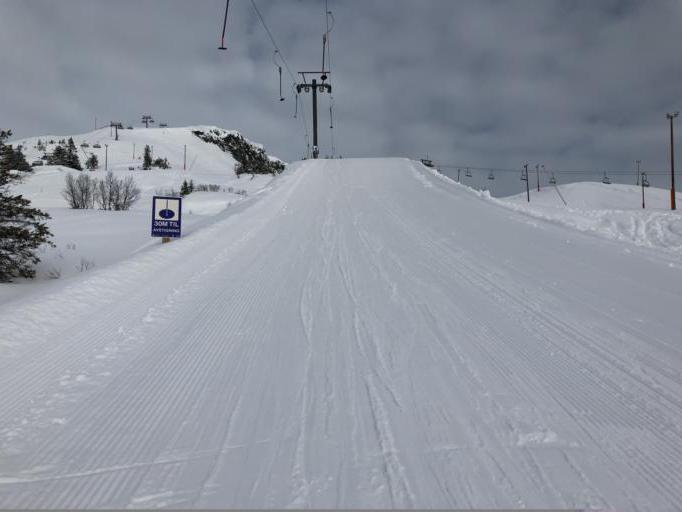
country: NO
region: Oppland
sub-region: Gausdal
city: Segalstad bru
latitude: 61.3427
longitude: 10.0879
